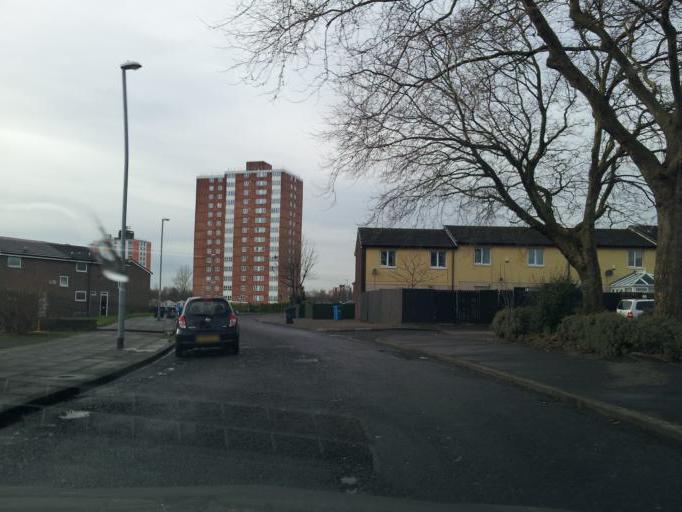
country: GB
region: England
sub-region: Manchester
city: Cheetham Hill
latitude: 53.5050
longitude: -2.2441
